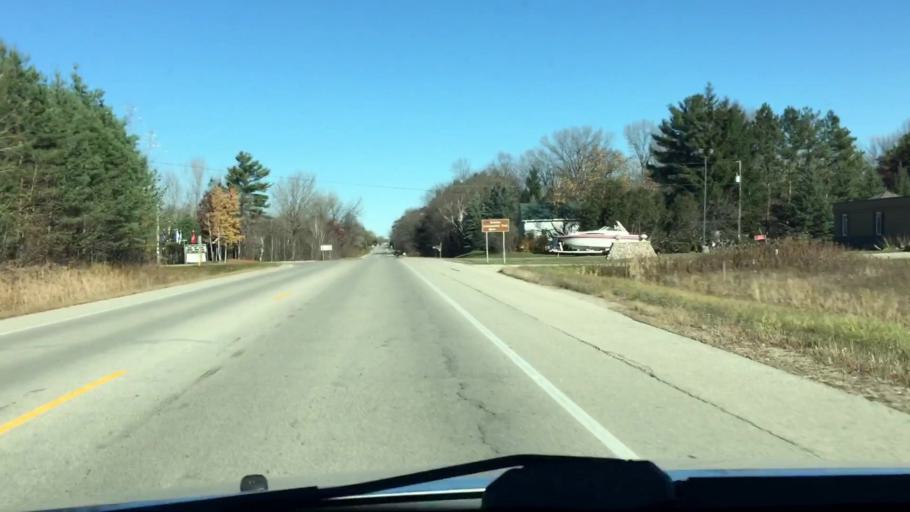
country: US
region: Wisconsin
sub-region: Brown County
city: Pulaski
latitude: 44.7570
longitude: -88.2507
